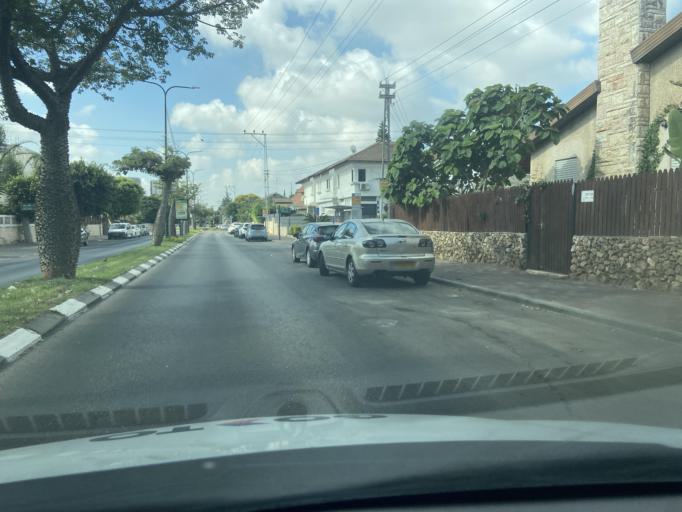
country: IL
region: Central District
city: Yehud
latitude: 32.0373
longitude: 34.8859
